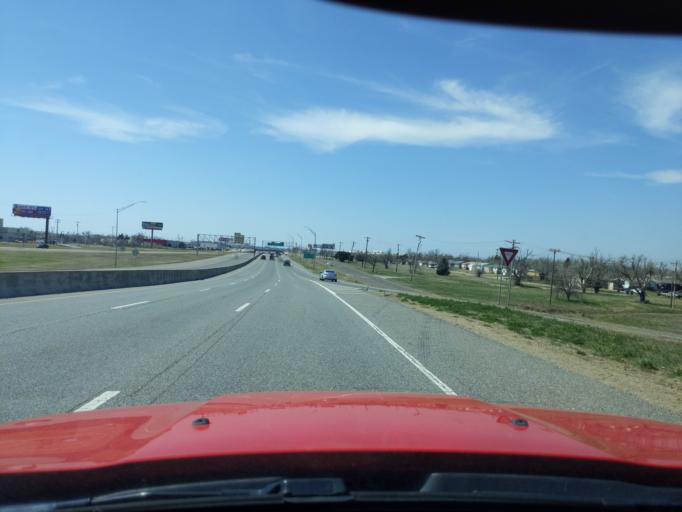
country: US
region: Oklahoma
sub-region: Cleveland County
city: Moore
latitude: 35.3921
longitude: -97.4969
